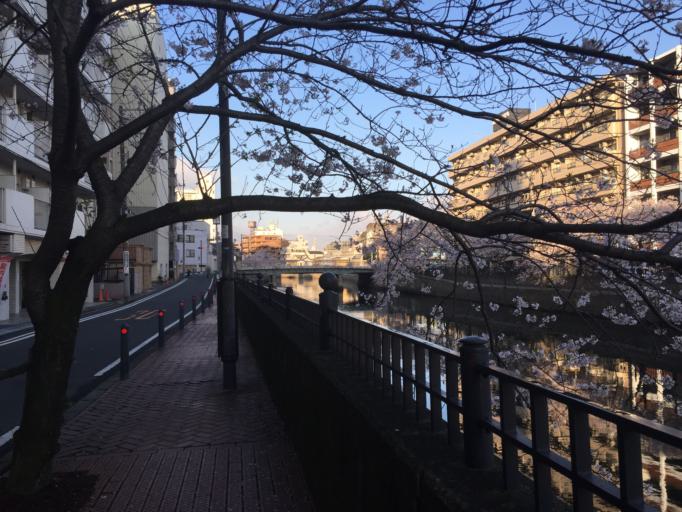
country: JP
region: Kanagawa
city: Yokohama
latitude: 35.4379
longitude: 139.6187
